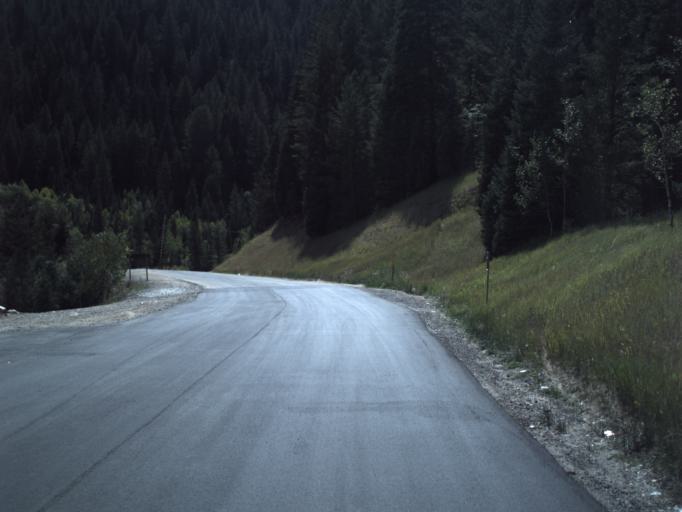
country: US
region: Utah
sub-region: Utah County
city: Highland
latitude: 40.4808
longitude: -111.6472
